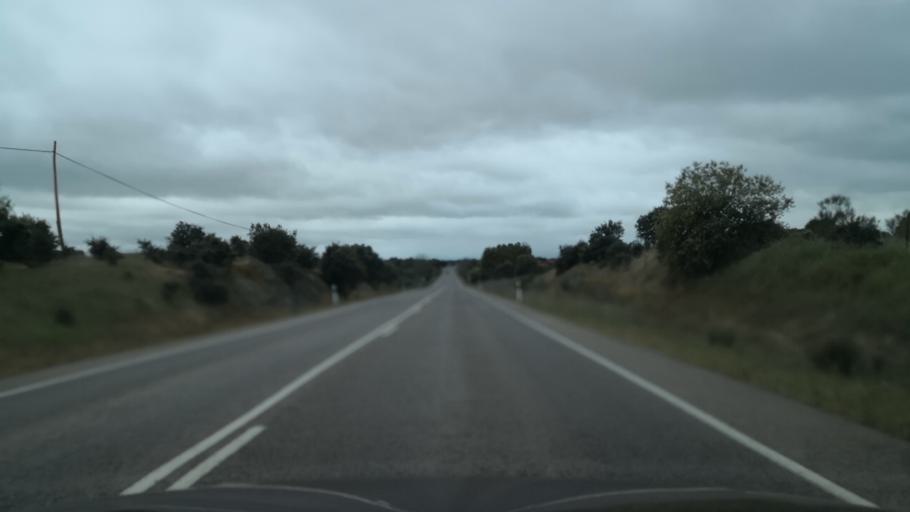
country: ES
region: Extremadura
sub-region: Provincia de Caceres
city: Caceres
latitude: 39.4179
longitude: -6.4136
